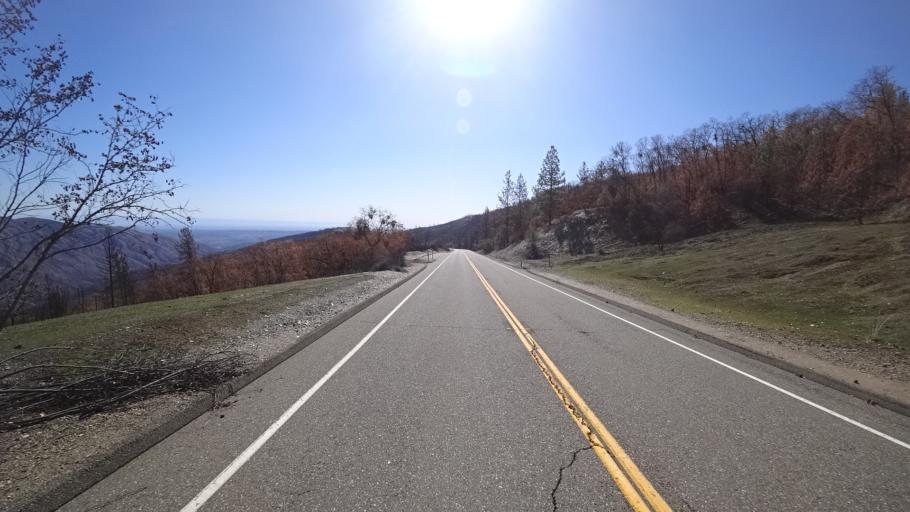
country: US
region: California
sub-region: Tehama County
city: Rancho Tehama Reserve
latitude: 39.6692
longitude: -122.6887
